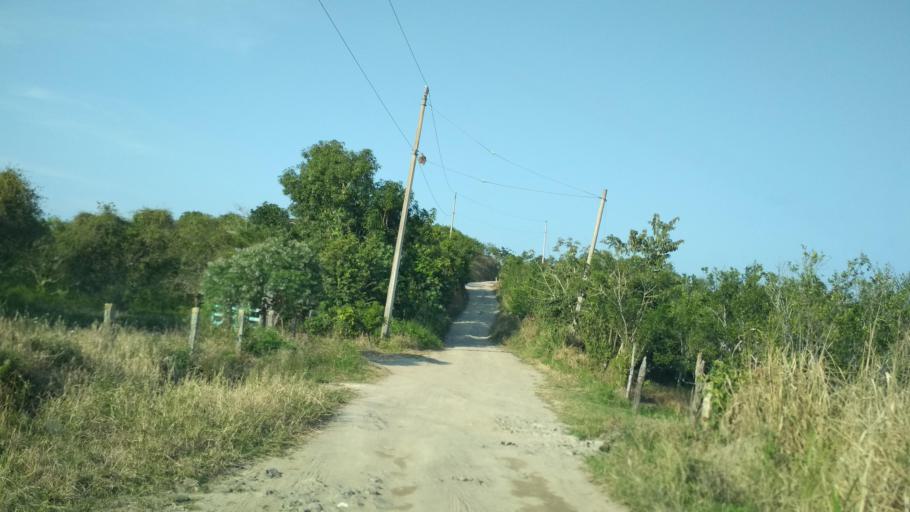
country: MX
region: Puebla
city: San Jose Acateno
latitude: 20.2212
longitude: -97.2621
